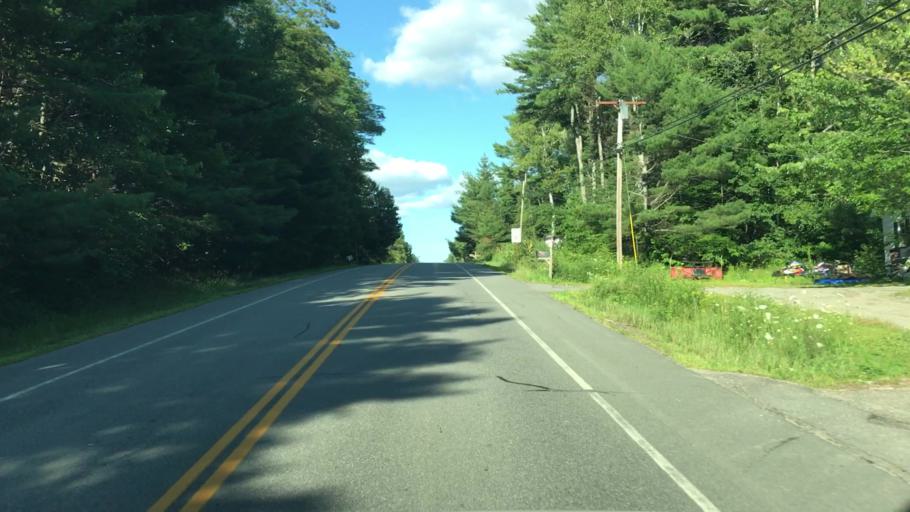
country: US
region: Maine
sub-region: Penobscot County
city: Lincoln
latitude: 45.3769
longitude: -68.4611
